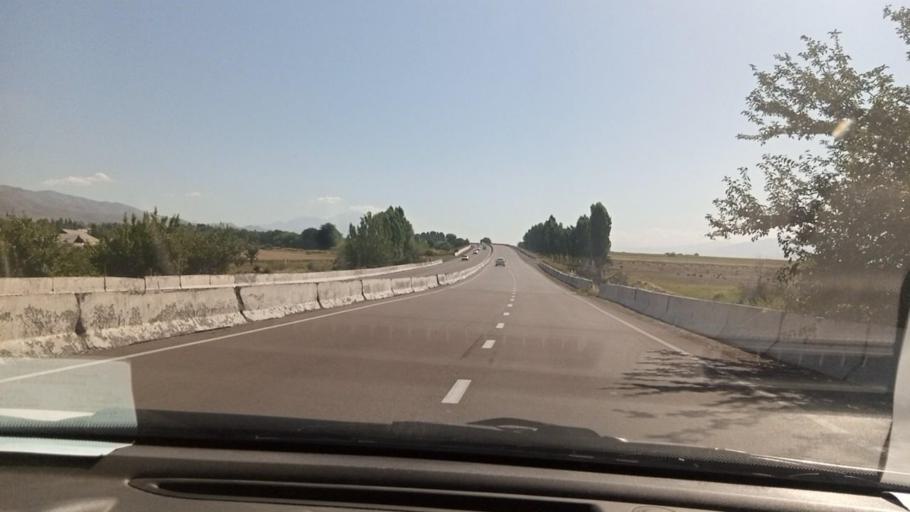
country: UZ
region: Toshkent
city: Angren
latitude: 40.9391
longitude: 69.9004
